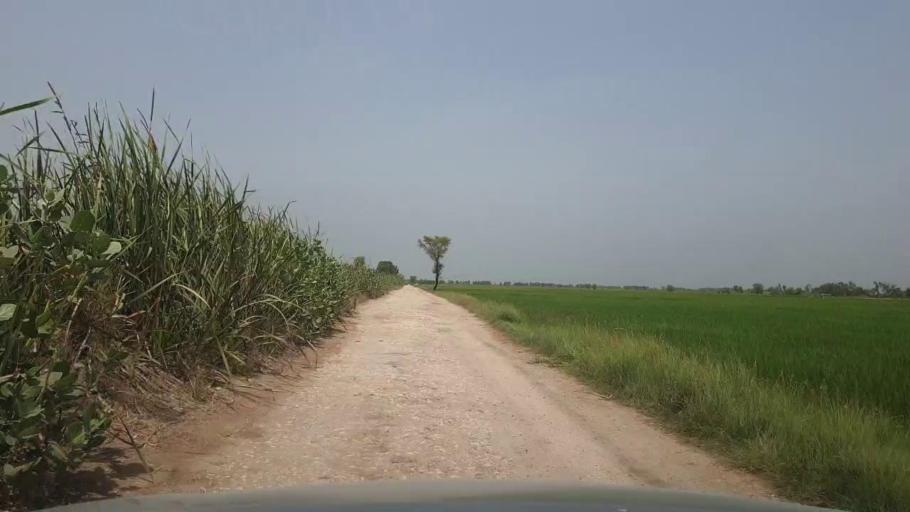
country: PK
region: Sindh
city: Garhi Yasin
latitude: 27.9342
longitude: 68.4319
